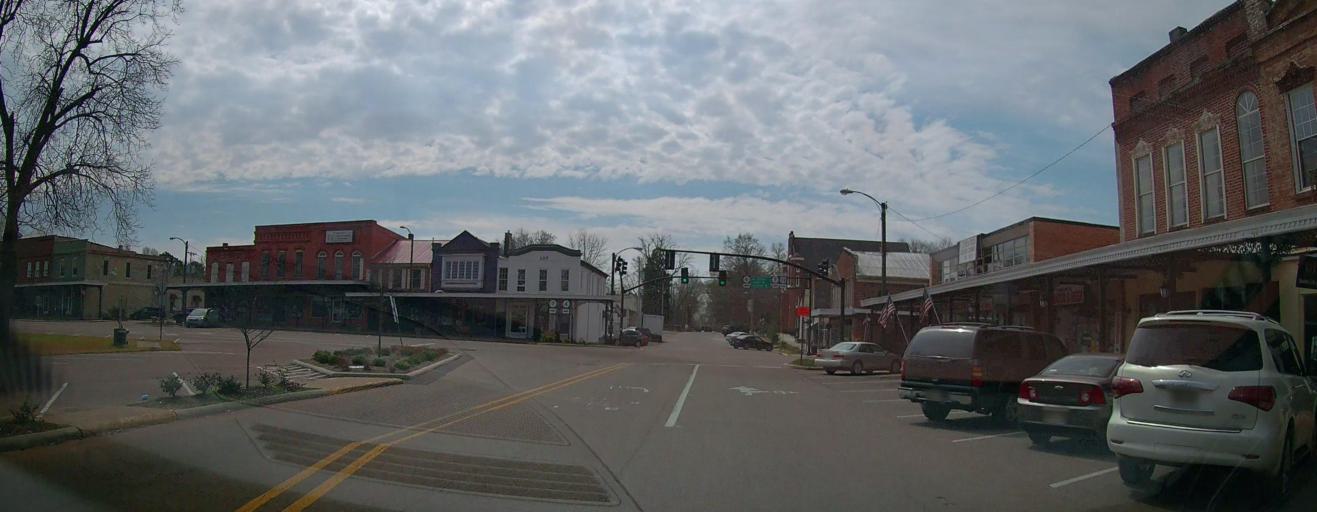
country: US
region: Mississippi
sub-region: Marshall County
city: Holly Springs
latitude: 34.7680
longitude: -89.4486
